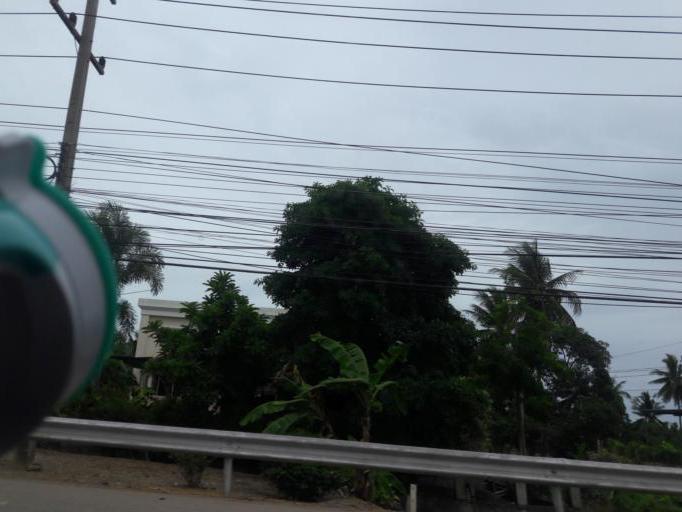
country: TH
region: Ratchaburi
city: Damnoen Saduak
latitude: 13.5490
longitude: 99.9670
